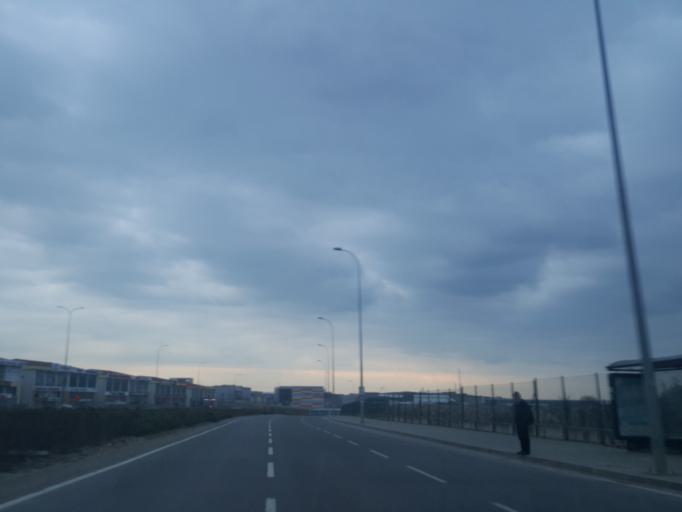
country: TR
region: Kocaeli
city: Tavsancil
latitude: 40.8310
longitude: 29.5703
